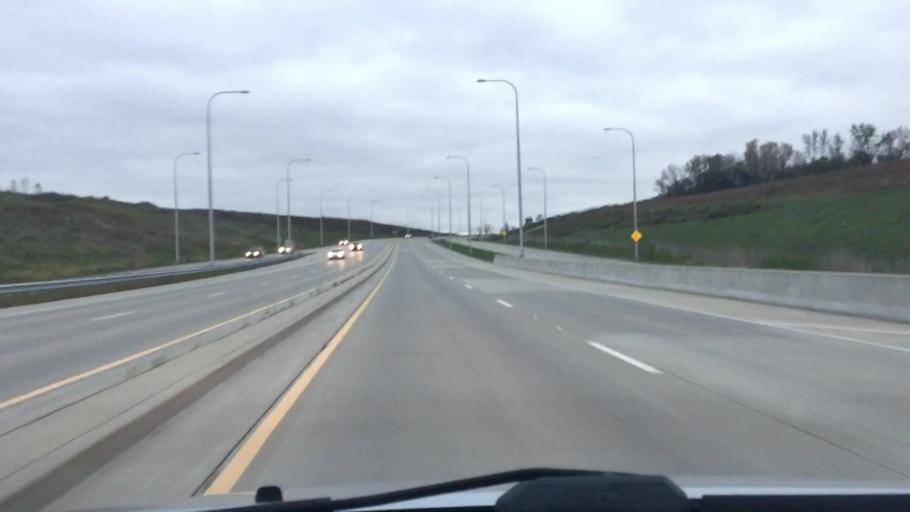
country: US
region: Illinois
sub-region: McHenry County
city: Algonquin
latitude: 42.1719
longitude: -88.2954
